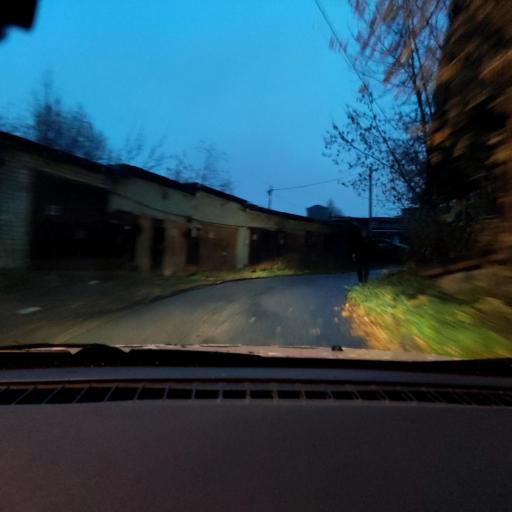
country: RU
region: Perm
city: Perm
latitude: 58.0248
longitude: 56.2826
